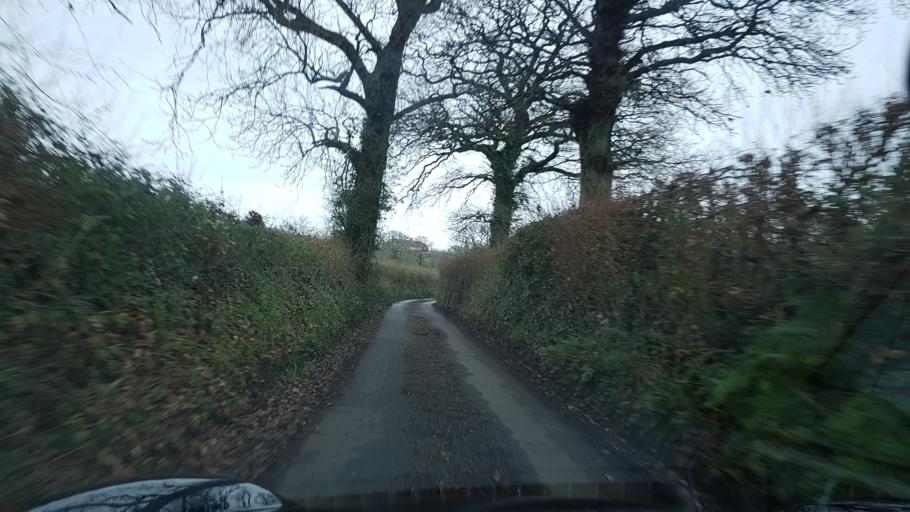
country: GB
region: England
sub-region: Somerset
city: Chard
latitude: 50.9109
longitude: -2.9637
